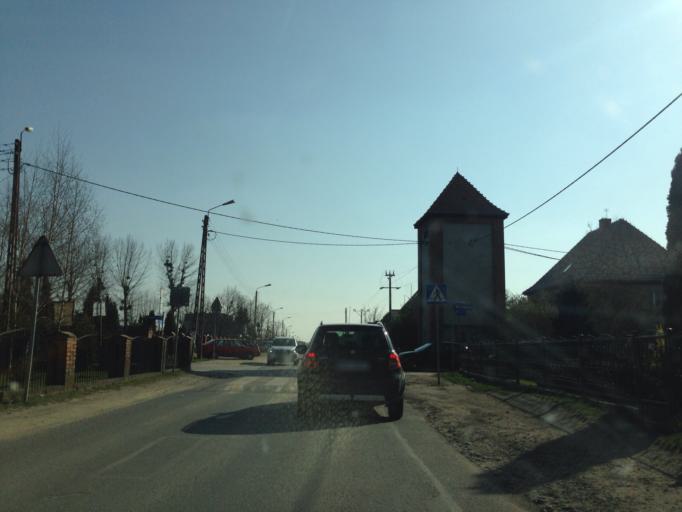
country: PL
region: Lower Silesian Voivodeship
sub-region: Powiat wroclawski
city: Kielczow
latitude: 51.1385
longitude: 17.1781
